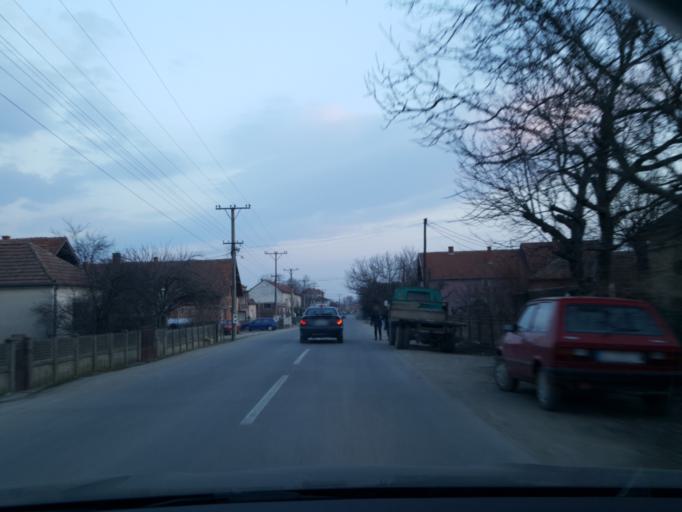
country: RS
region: Central Serbia
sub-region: Nisavski Okrug
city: Aleksinac
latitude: 43.5021
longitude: 21.7014
